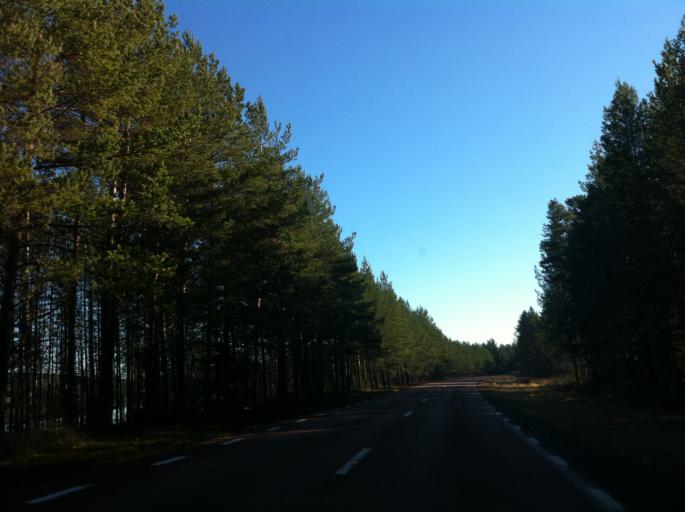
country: SE
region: Dalarna
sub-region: Alvdalens Kommun
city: AElvdalen
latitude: 61.3050
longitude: 13.7244
